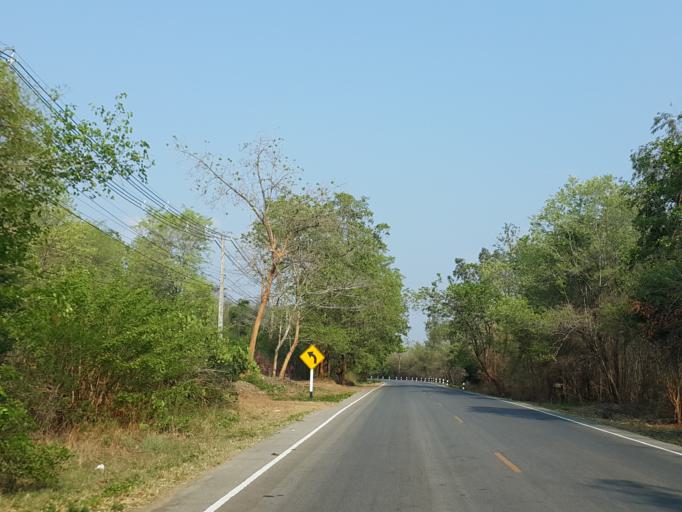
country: TH
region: Kanchanaburi
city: Sai Yok
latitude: 14.2197
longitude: 99.1755
